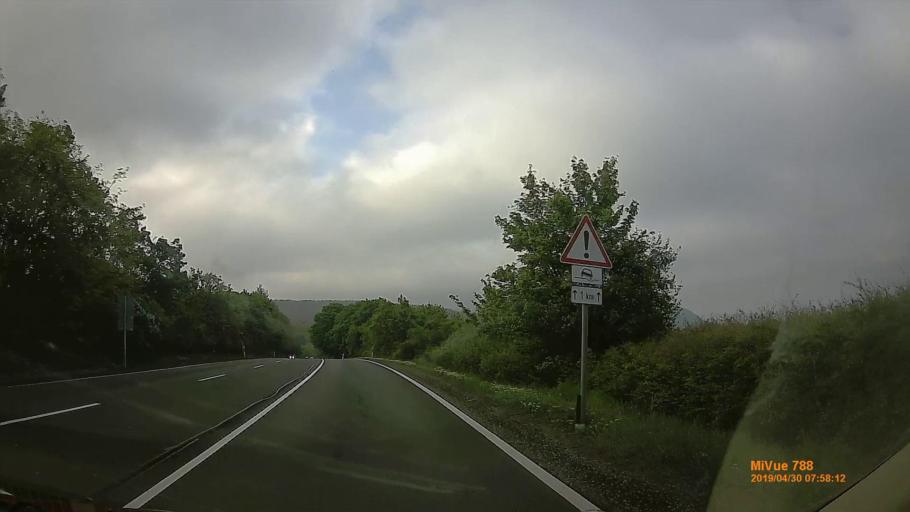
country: HU
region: Nograd
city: Retsag
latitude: 47.8728
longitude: 19.1067
